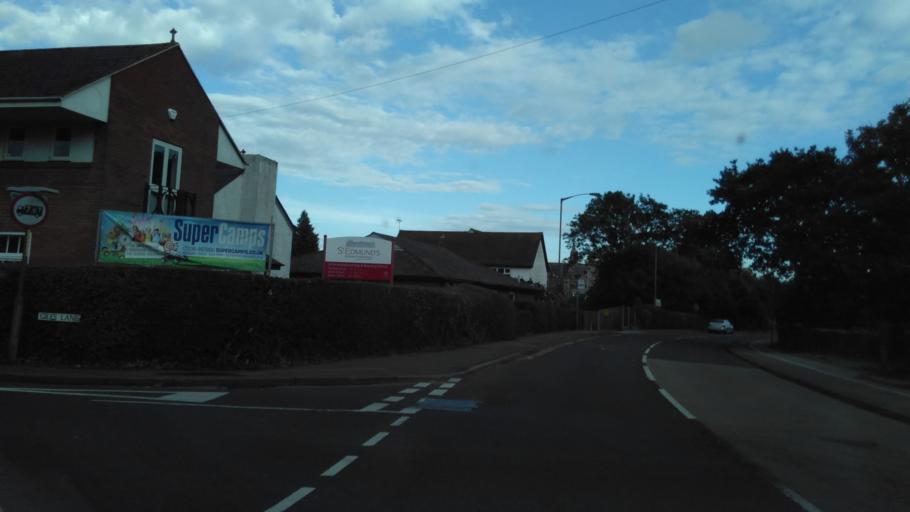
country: GB
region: England
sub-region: Kent
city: Blean
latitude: 51.2932
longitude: 1.0571
